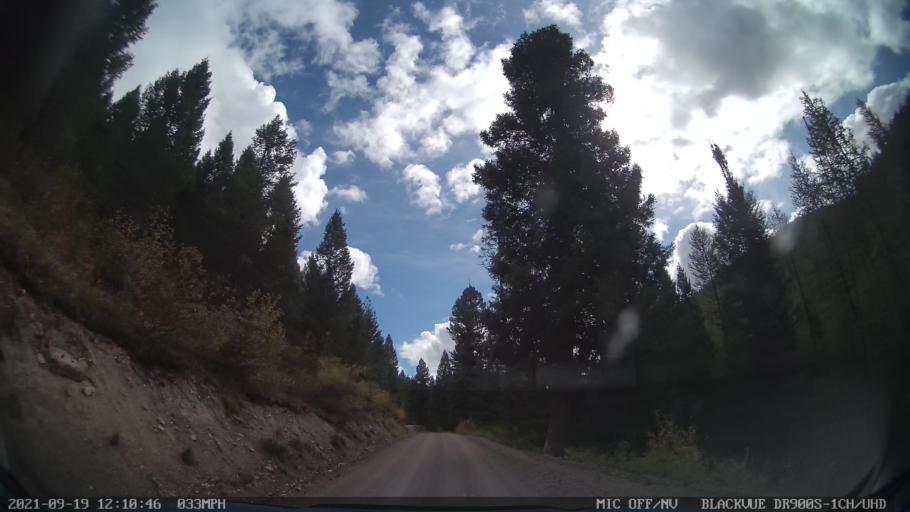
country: US
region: Montana
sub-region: Missoula County
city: Seeley Lake
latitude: 47.1773
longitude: -113.3802
